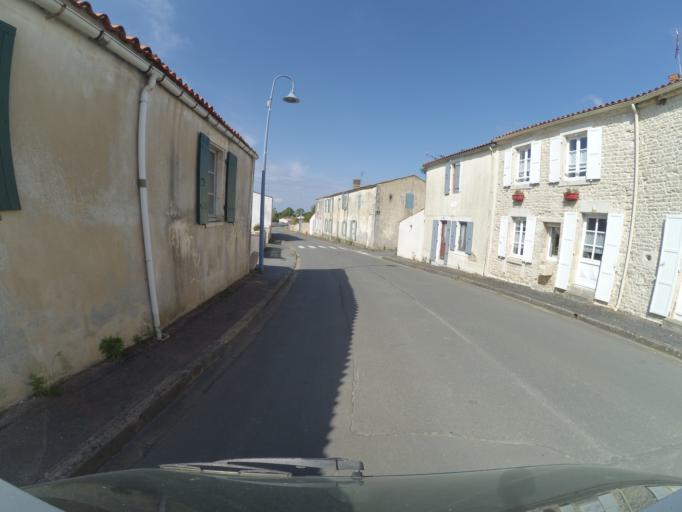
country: FR
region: Poitou-Charentes
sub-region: Departement de la Charente-Maritime
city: Andilly
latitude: 46.2422
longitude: -1.0659
